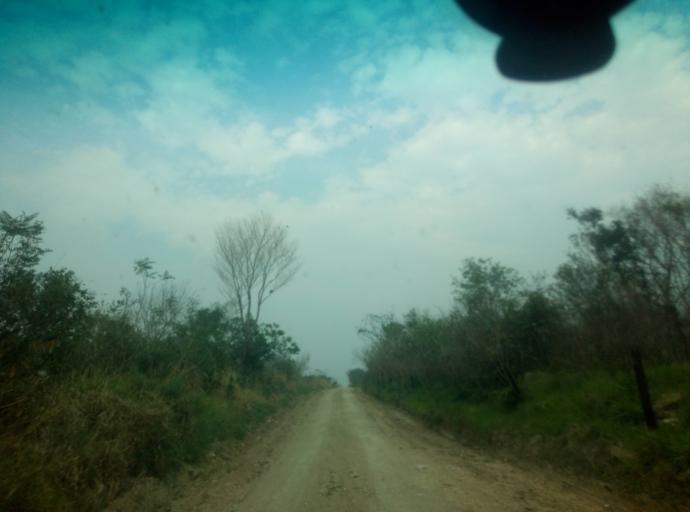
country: PY
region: Caaguazu
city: San Joaquin
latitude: -25.0991
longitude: -56.1353
